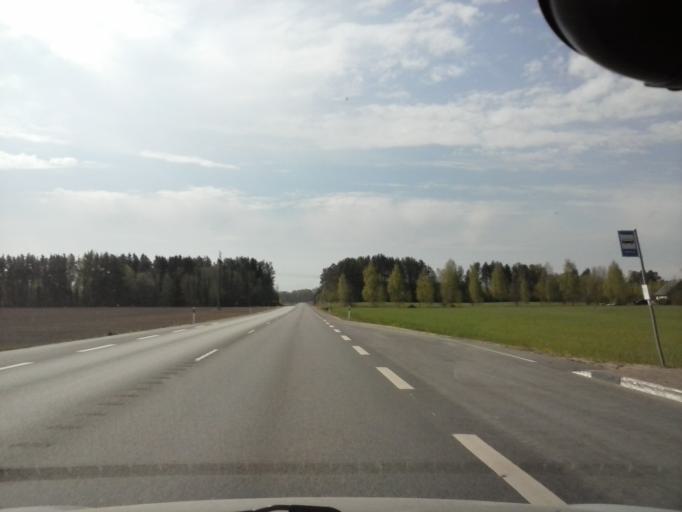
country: EE
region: Tartu
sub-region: UElenurme vald
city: Ulenurme
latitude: 58.2175
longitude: 26.7036
